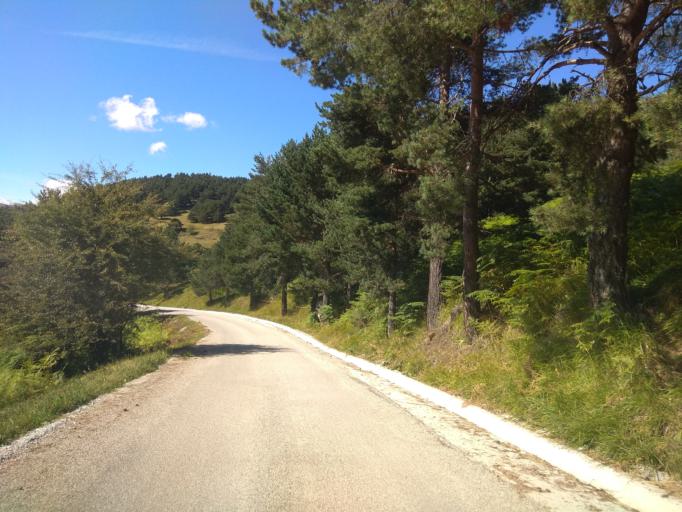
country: ES
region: Catalonia
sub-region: Provincia de Lleida
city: Les
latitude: 42.7623
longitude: 0.7137
